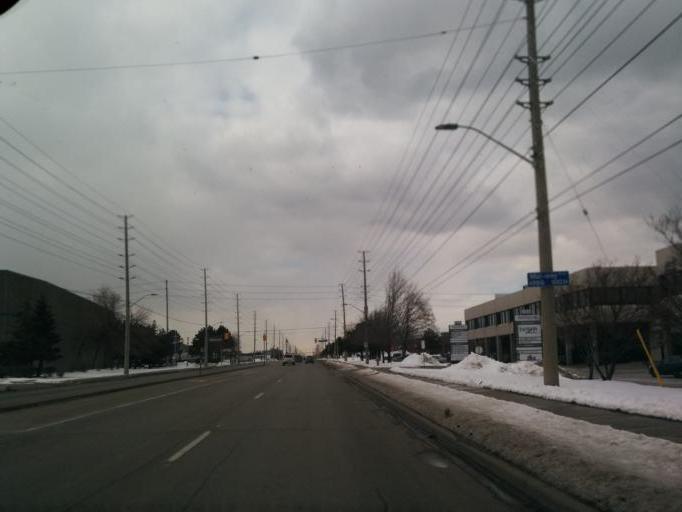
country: CA
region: Ontario
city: Mississauga
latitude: 43.6591
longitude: -79.6760
